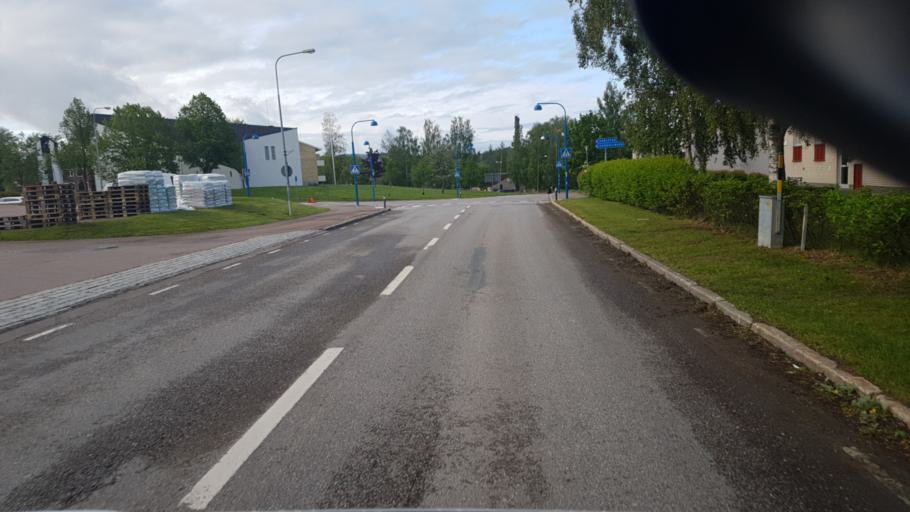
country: SE
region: Vaermland
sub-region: Eda Kommun
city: Amotfors
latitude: 59.7633
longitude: 12.3607
